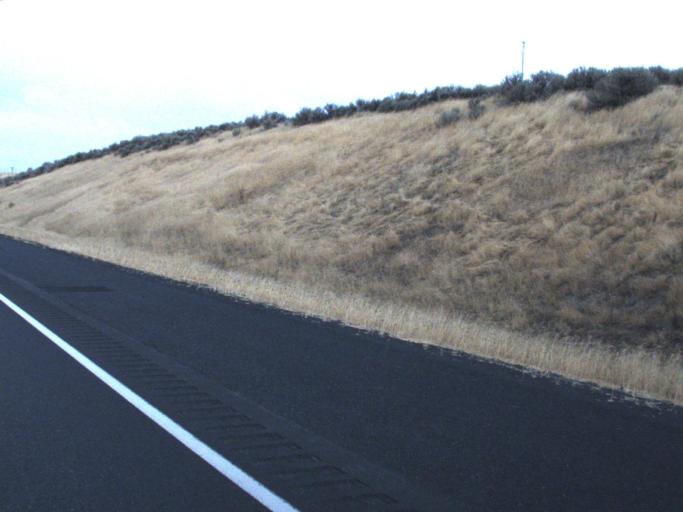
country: US
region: Washington
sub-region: Grant County
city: Warden
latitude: 47.0875
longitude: -118.9314
